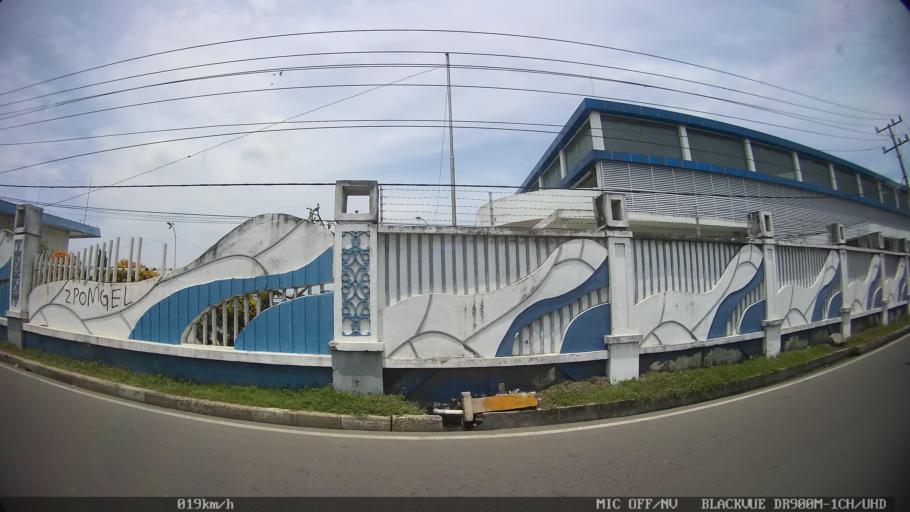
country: ID
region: North Sumatra
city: Belawan
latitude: 3.7796
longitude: 98.6816
